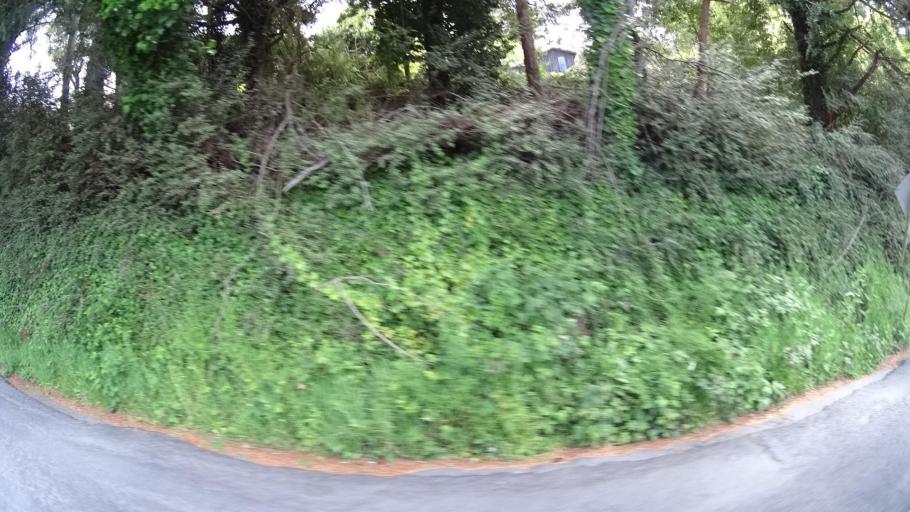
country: US
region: California
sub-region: Humboldt County
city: Bayside
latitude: 40.8482
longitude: -124.0626
